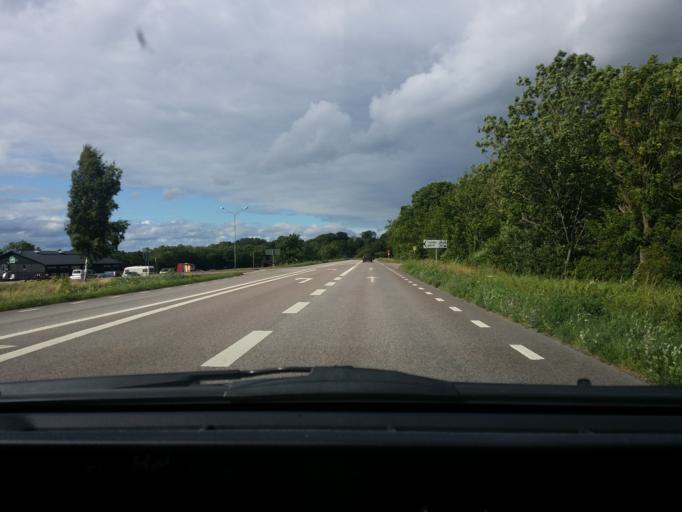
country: SE
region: Kalmar
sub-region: Borgholms Kommun
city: Borgholm
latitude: 56.9047
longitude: 16.7342
